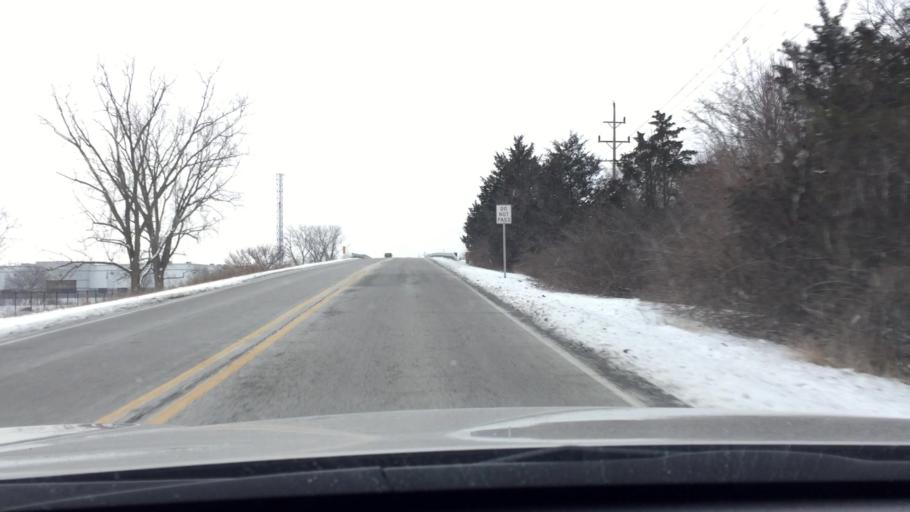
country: US
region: Indiana
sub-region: Hamilton County
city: Fishers
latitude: 39.9689
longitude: -85.9942
